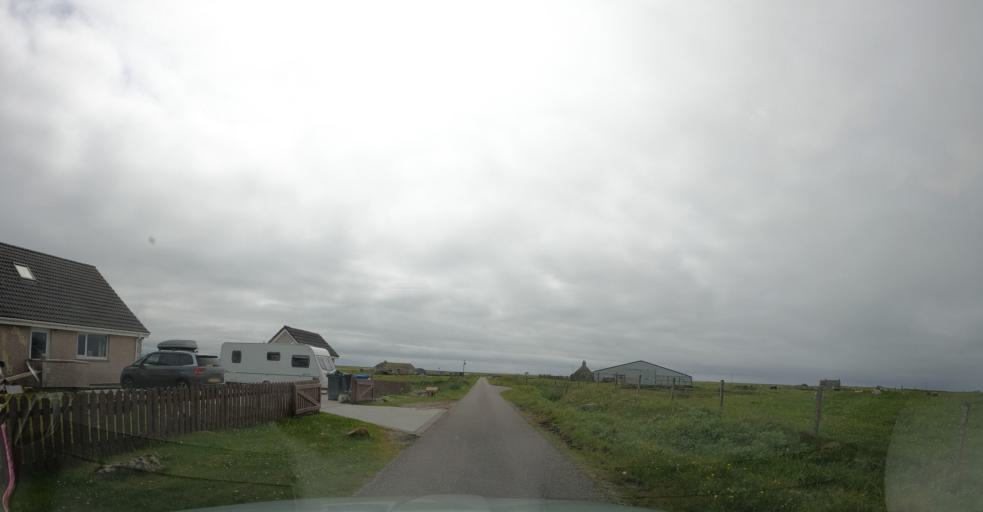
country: GB
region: Scotland
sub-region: Eilean Siar
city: Isle of North Uist
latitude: 57.5294
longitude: -7.3600
